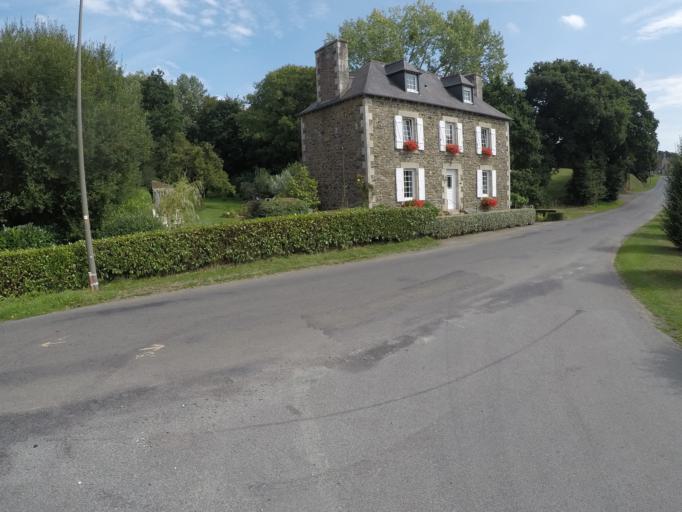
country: FR
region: Brittany
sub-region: Departement des Cotes-d'Armor
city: Goudelin
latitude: 48.6099
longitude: -3.0198
